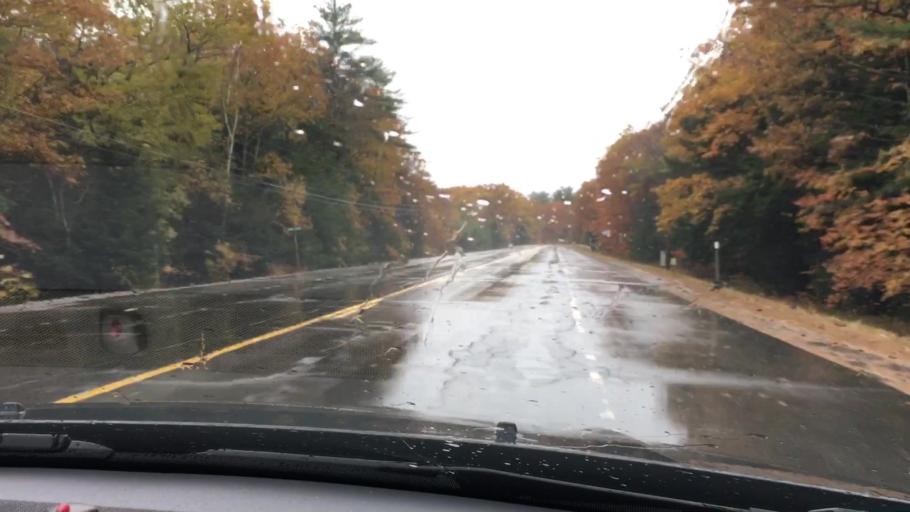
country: US
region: New Hampshire
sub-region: Grafton County
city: Ashland
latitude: 43.7153
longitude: -71.6249
